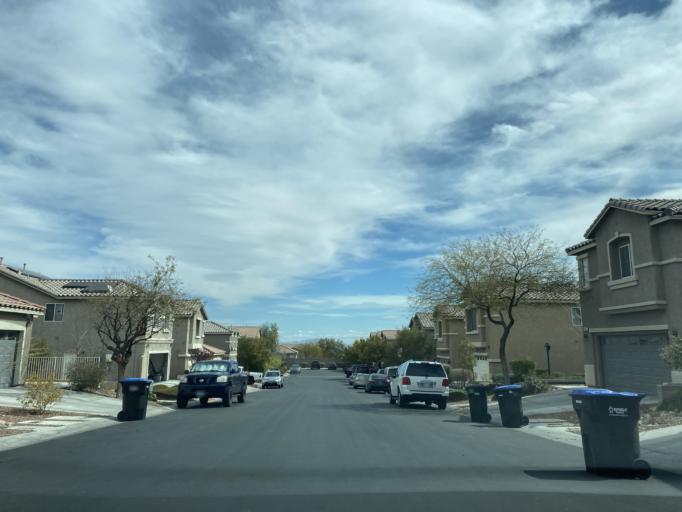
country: US
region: Nevada
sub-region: Clark County
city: Summerlin South
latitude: 36.3051
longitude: -115.3049
